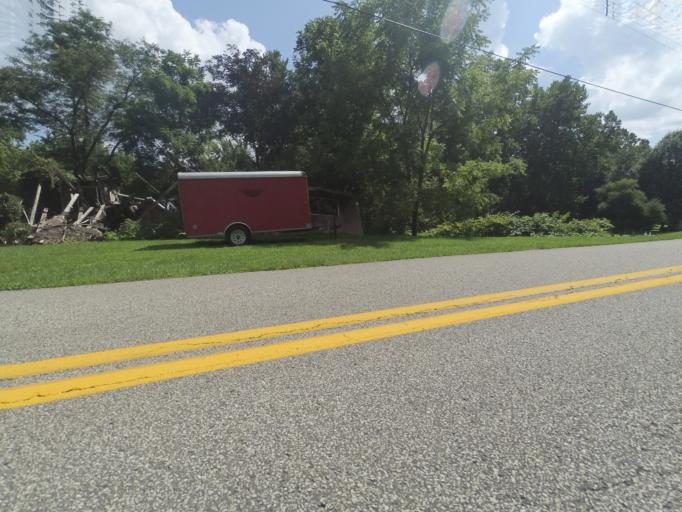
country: US
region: West Virginia
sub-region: Cabell County
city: Pea Ridge
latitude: 38.4280
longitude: -82.3155
